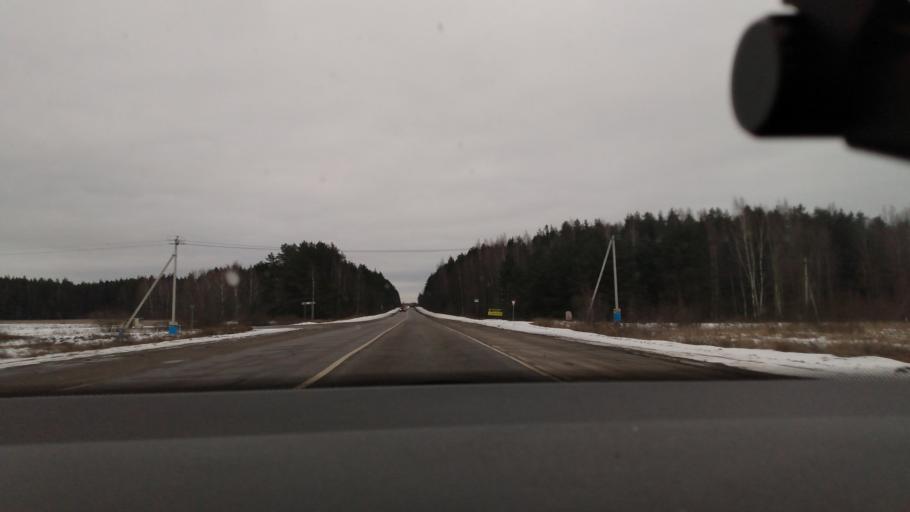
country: RU
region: Moskovskaya
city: Yegor'yevsk
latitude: 55.4335
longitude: 39.0270
